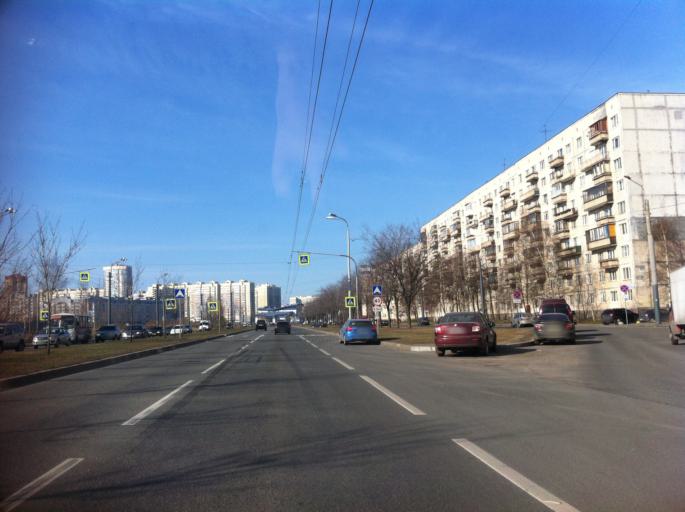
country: RU
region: St.-Petersburg
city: Uritsk
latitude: 59.8527
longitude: 30.1760
